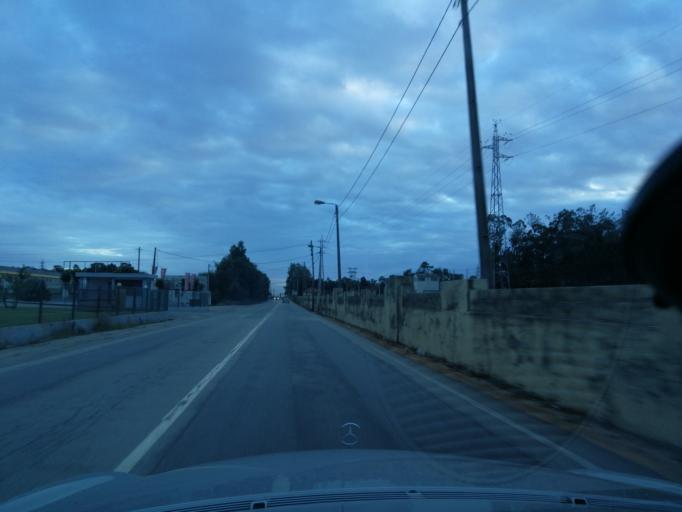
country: PT
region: Aveiro
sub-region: Estarreja
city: Beduido
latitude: 40.7786
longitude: -8.5669
